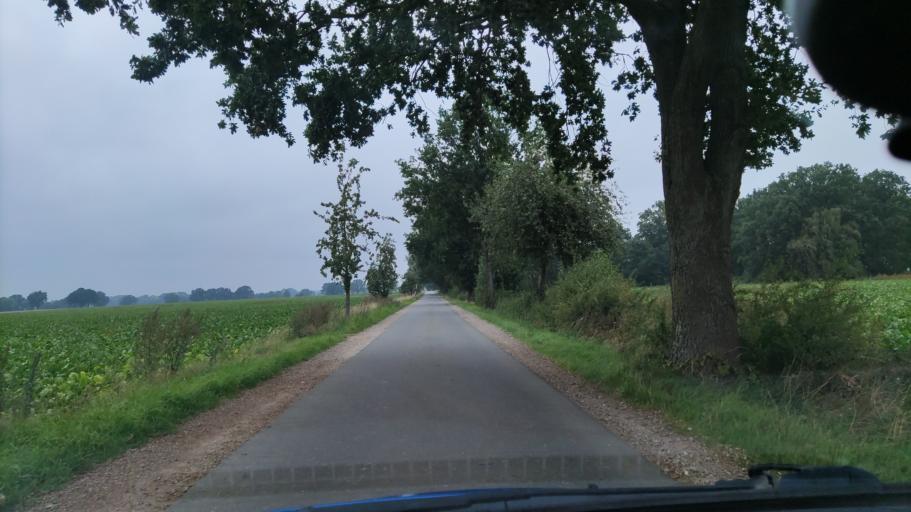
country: DE
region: Lower Saxony
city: Altenmedingen
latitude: 53.1216
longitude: 10.6272
